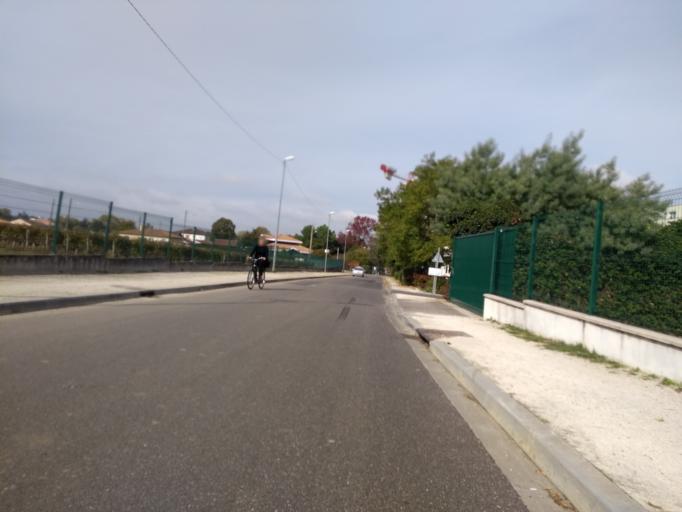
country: FR
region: Aquitaine
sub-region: Departement de la Gironde
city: Talence
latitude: 44.8183
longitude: -0.6070
